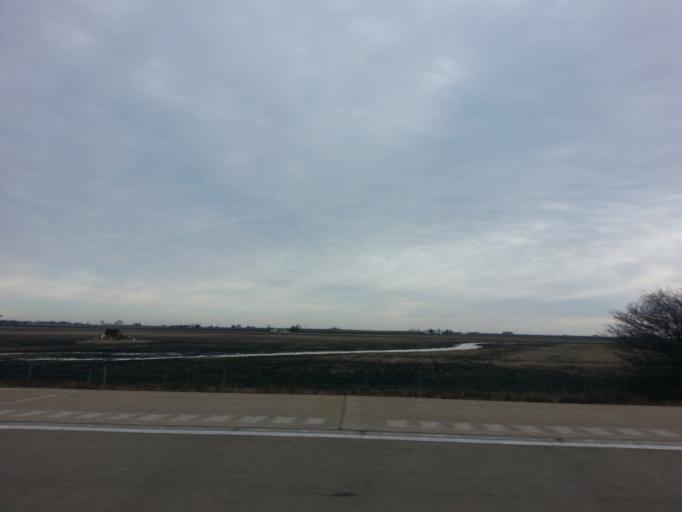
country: US
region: Illinois
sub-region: Woodford County
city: El Paso
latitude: 40.7107
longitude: -89.0301
